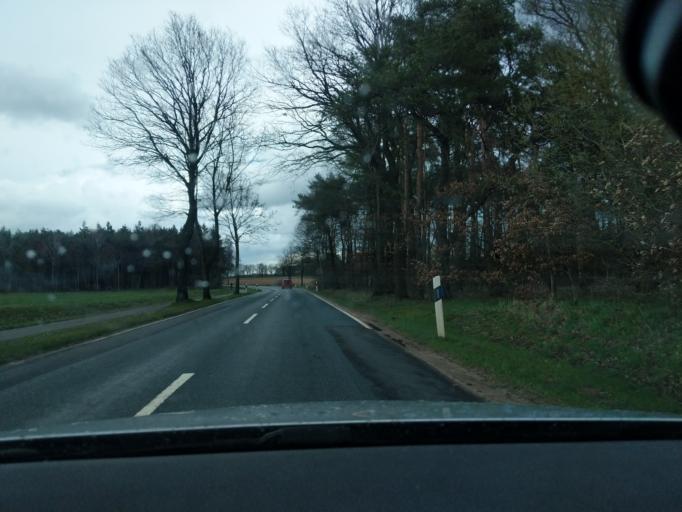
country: DE
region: Lower Saxony
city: Kutenholz
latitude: 53.5034
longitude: 9.3538
